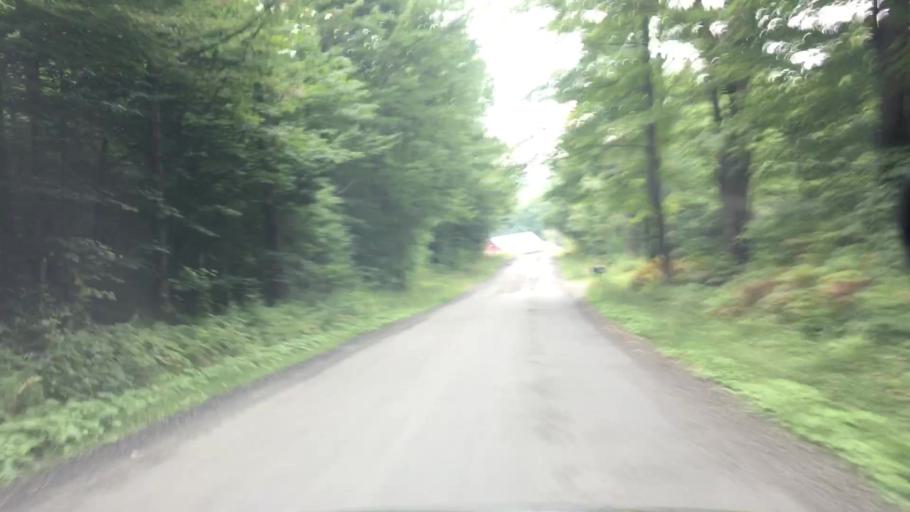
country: US
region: Vermont
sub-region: Windham County
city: Dover
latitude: 42.8354
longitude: -72.8041
